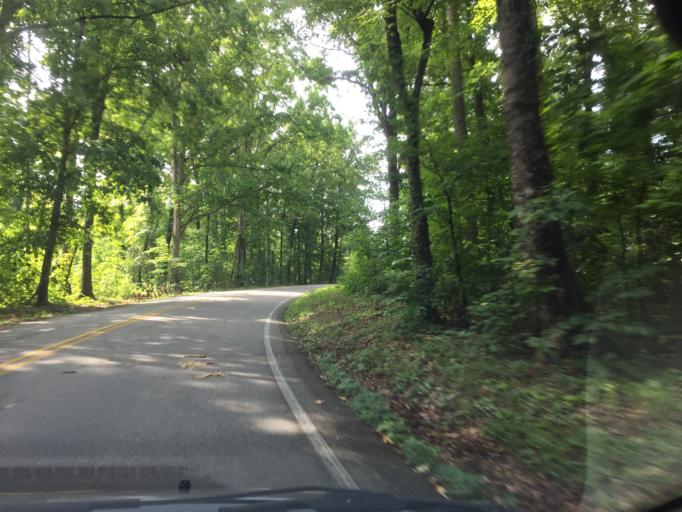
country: US
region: Tennessee
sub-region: Hamilton County
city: Apison
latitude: 35.0143
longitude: -85.0541
